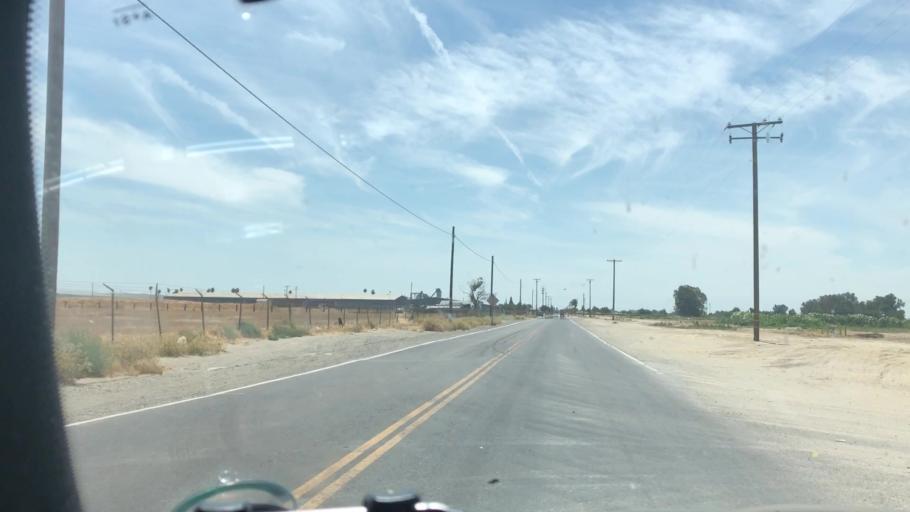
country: US
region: California
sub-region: Fresno County
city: Easton
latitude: 36.6845
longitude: -119.7548
